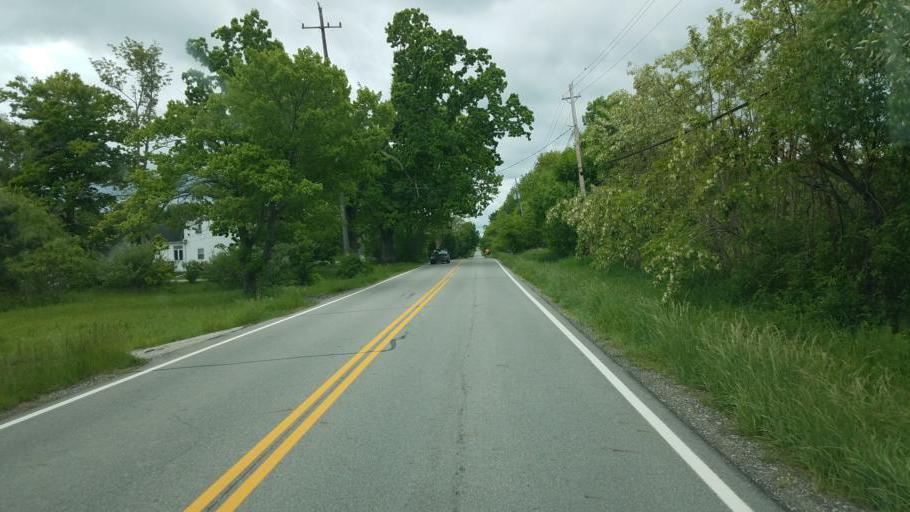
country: US
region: Ohio
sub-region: Portage County
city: Hiram
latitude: 41.3913
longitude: -81.1716
